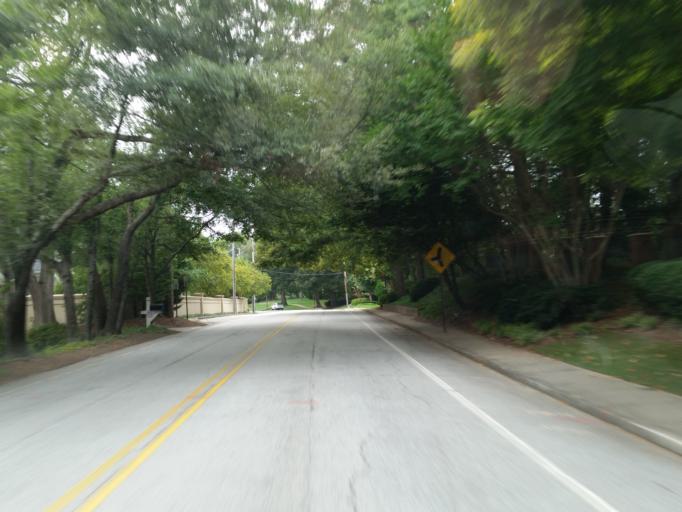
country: US
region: Georgia
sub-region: Cobb County
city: Vinings
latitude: 33.8392
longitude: -84.4238
